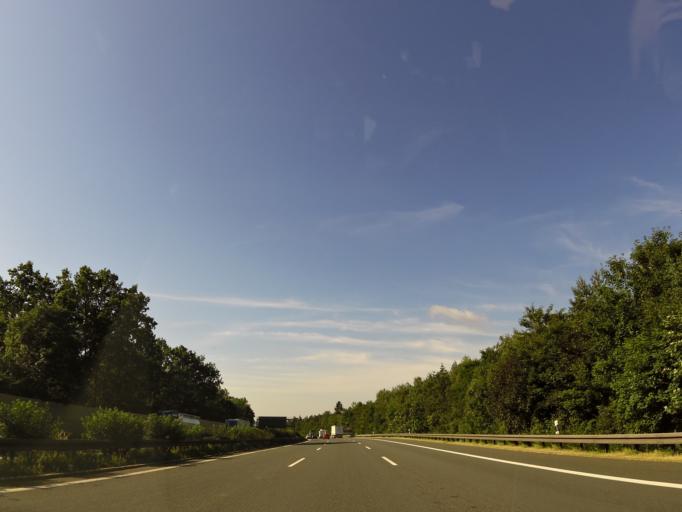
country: DE
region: Bavaria
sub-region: Regierungsbezirk Mittelfranken
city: Feucht
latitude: 49.3814
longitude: 11.2004
